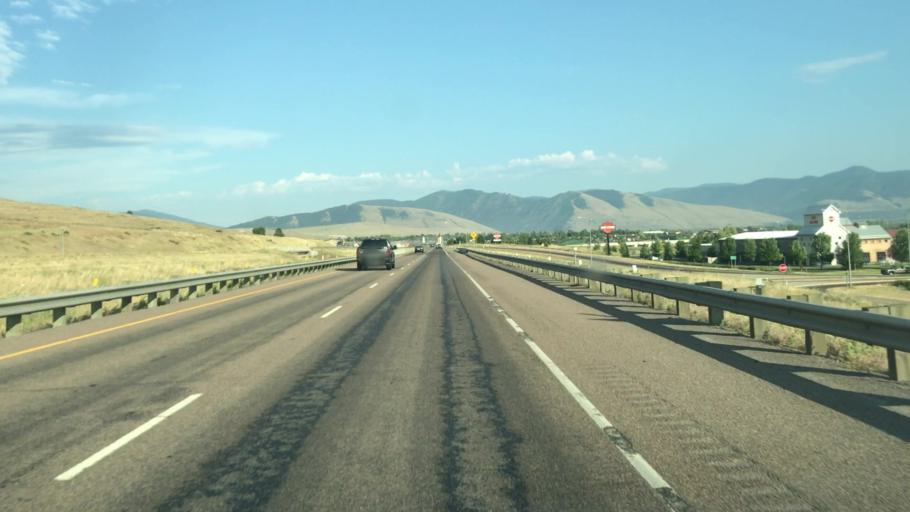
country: US
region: Montana
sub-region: Missoula County
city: Orchard Homes
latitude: 46.9242
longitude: -114.0701
